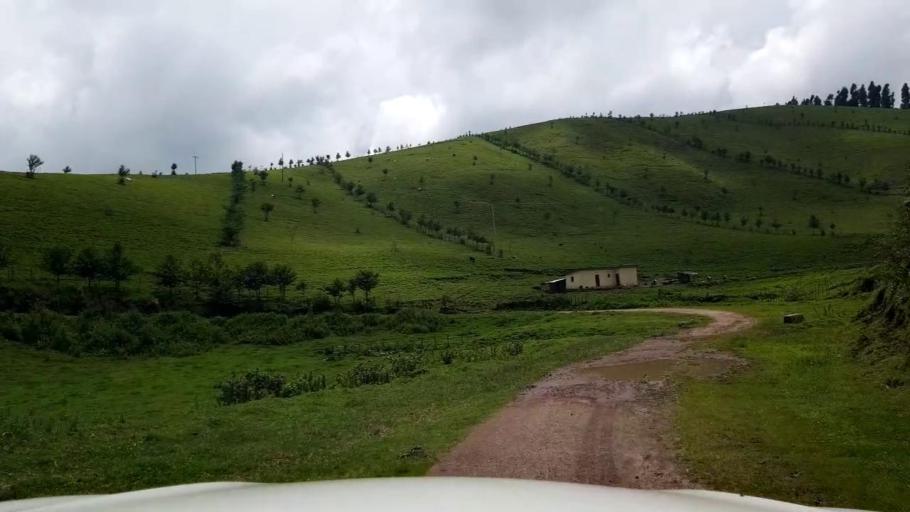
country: RW
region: Western Province
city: Gisenyi
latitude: -1.6878
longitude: 29.4227
